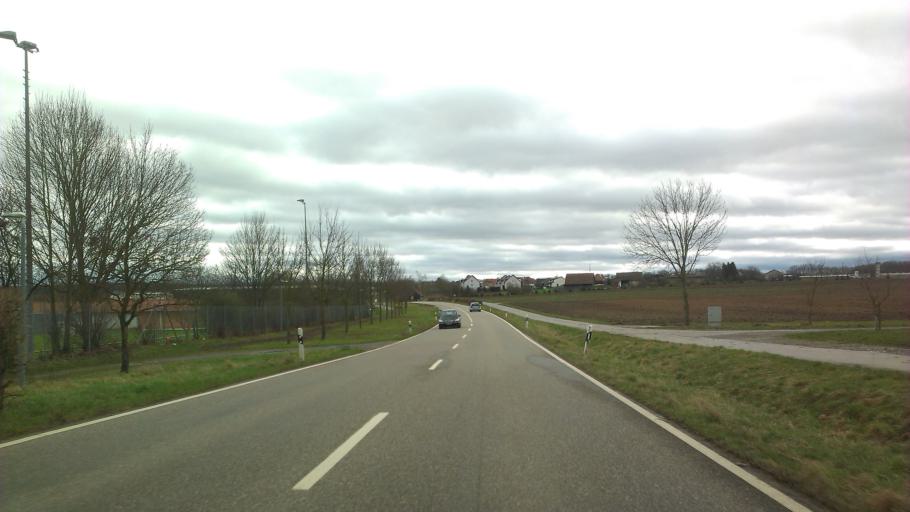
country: DE
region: Baden-Wuerttemberg
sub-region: Regierungsbezirk Stuttgart
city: Sersheim
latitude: 48.9656
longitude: 9.0043
